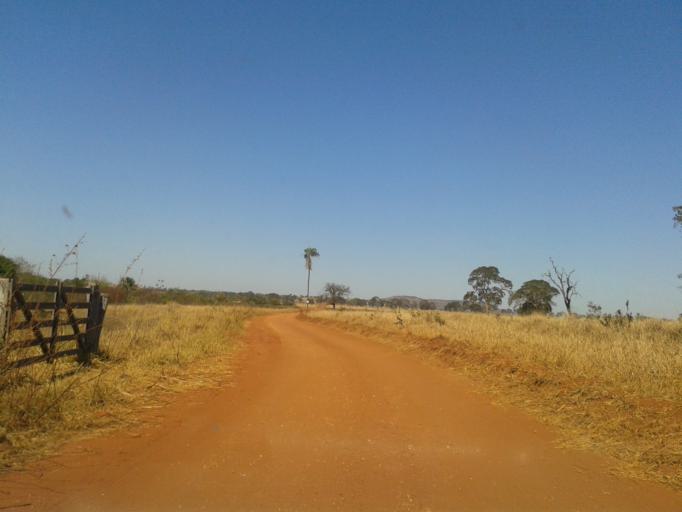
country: BR
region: Minas Gerais
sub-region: Santa Vitoria
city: Santa Vitoria
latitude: -19.1509
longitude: -50.1565
